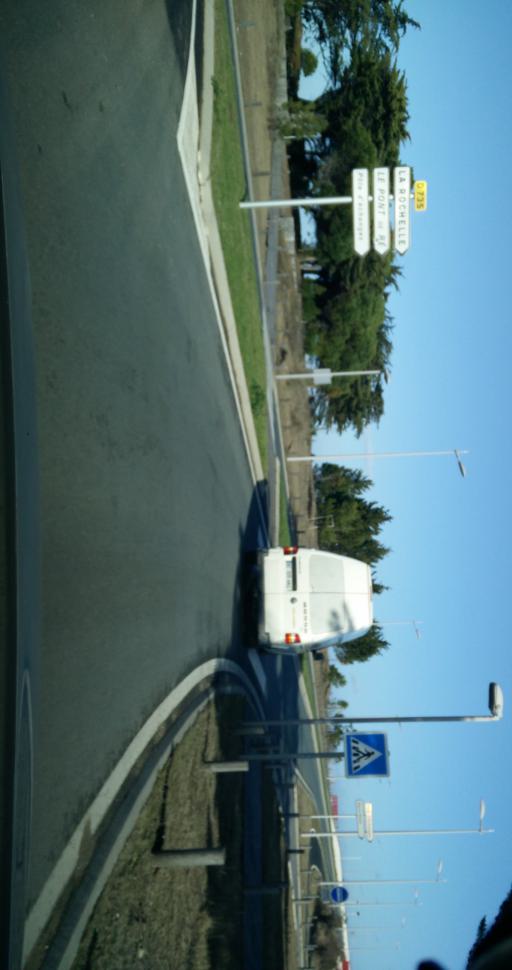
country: FR
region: Poitou-Charentes
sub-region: Departement de la Charente-Maritime
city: Rivedoux-Plage
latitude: 46.1623
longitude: -1.2579
